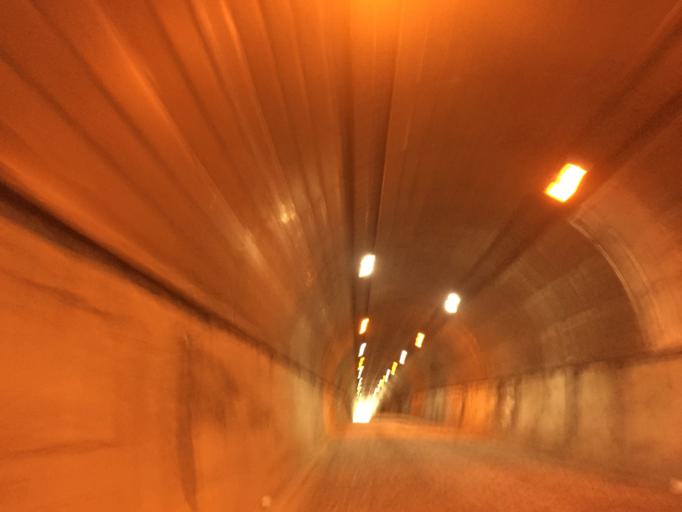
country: JP
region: Shizuoka
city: Numazu
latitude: 35.0257
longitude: 138.9102
